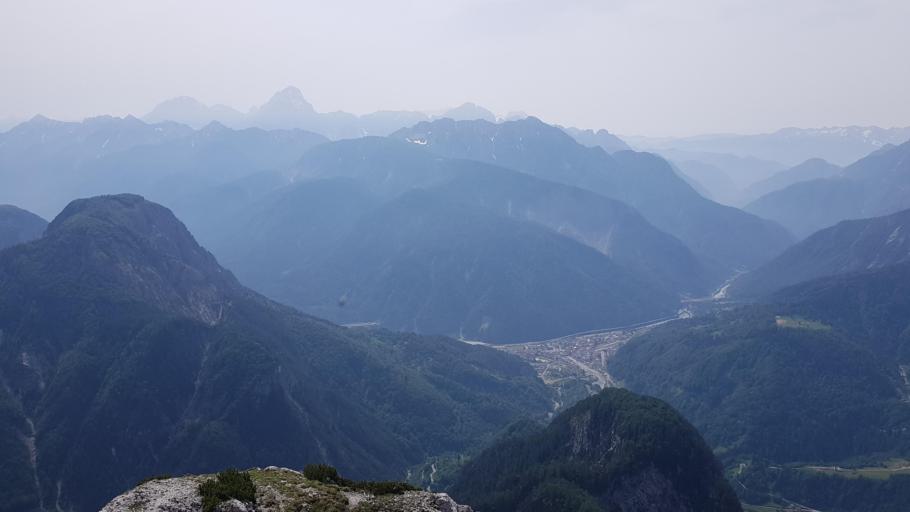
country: IT
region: Friuli Venezia Giulia
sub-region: Provincia di Udine
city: Pontebba
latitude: 46.5380
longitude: 13.2858
